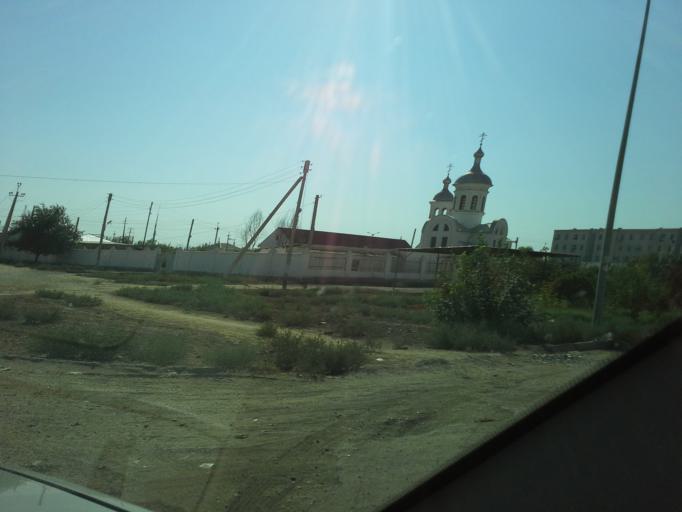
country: TM
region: Dasoguz
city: Dasoguz
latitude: 41.8228
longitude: 59.9669
